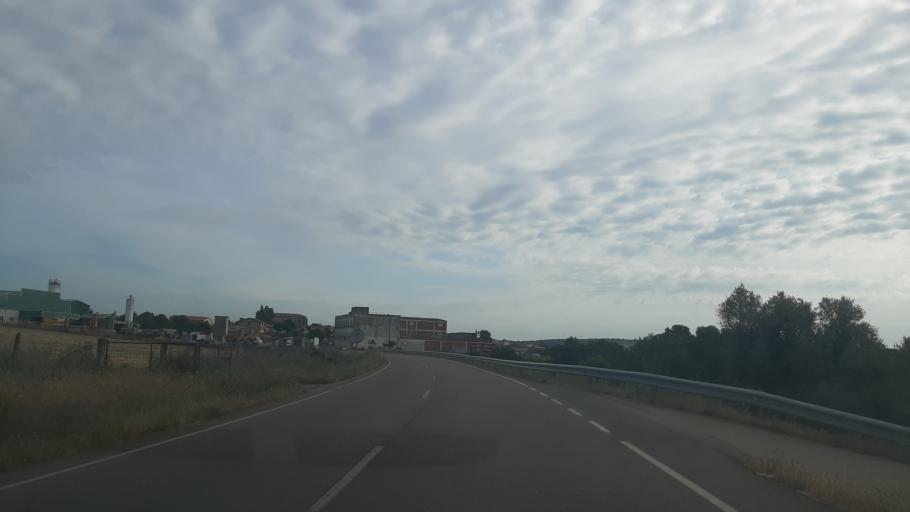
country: ES
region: Castille and Leon
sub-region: Provincia de Salamanca
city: Gallegos de Arganan
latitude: 40.6243
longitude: -6.7038
